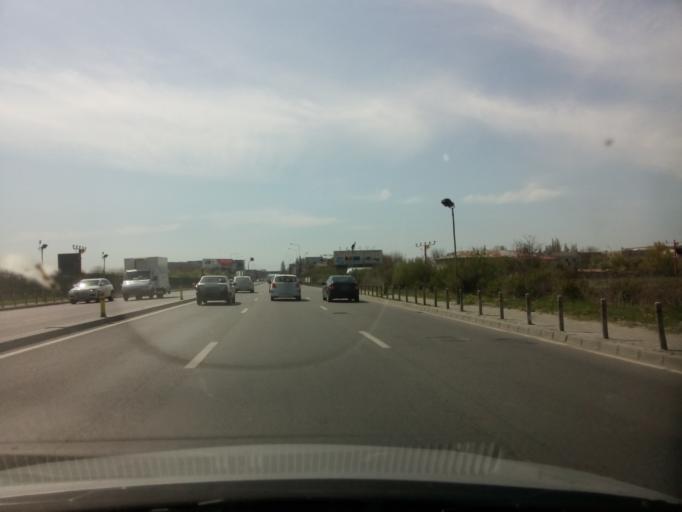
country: RO
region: Ilfov
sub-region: Comuna Otopeni
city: Otopeni
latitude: 44.5646
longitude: 26.0696
